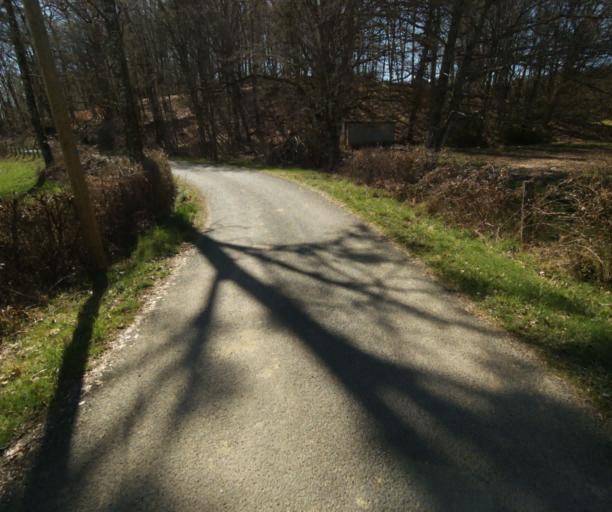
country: FR
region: Limousin
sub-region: Departement de la Correze
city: Saint-Clement
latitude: 45.3191
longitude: 1.6949
